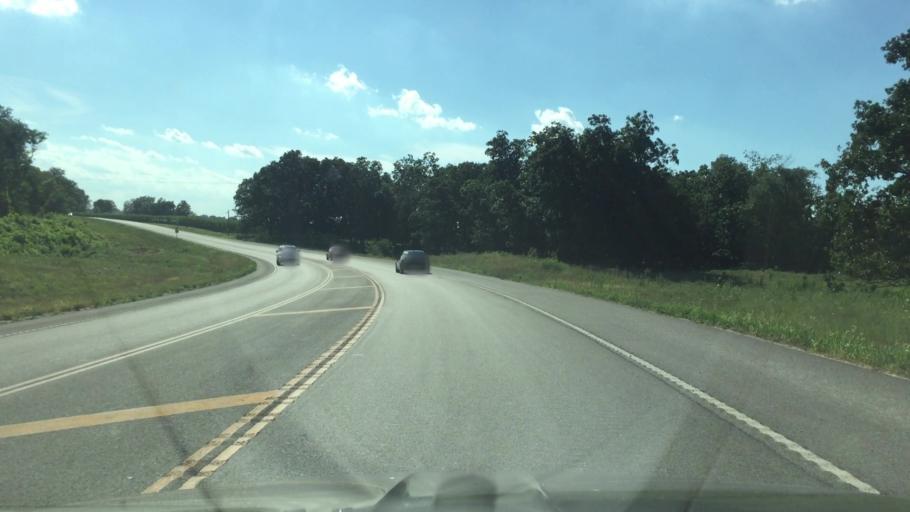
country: US
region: Missouri
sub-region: Morgan County
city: Versailles
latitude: 38.4484
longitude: -92.7977
